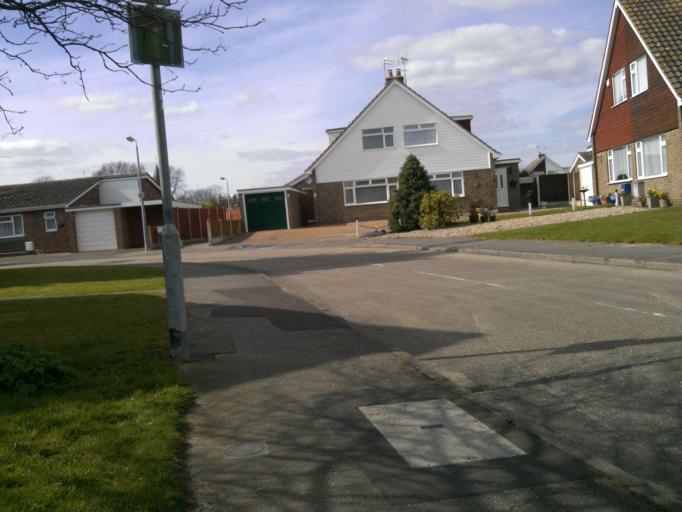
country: GB
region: England
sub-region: Essex
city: Clacton-on-Sea
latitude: 51.8049
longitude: 1.1599
